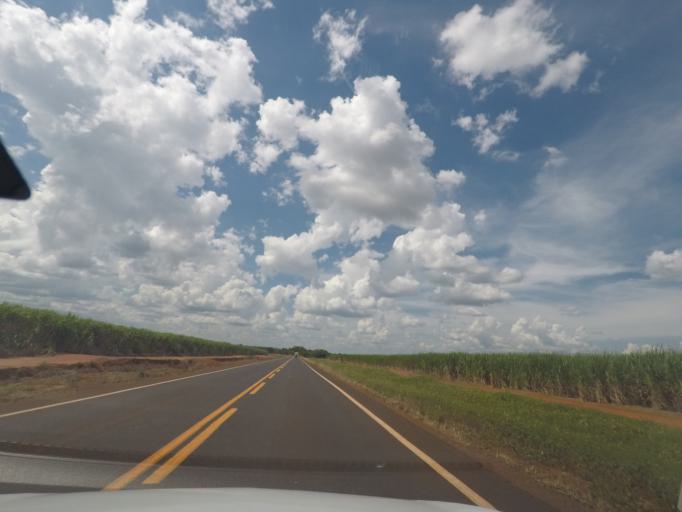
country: BR
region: Minas Gerais
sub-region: Conceicao Das Alagoas
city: Conceicao das Alagoas
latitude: -19.8382
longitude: -48.5908
